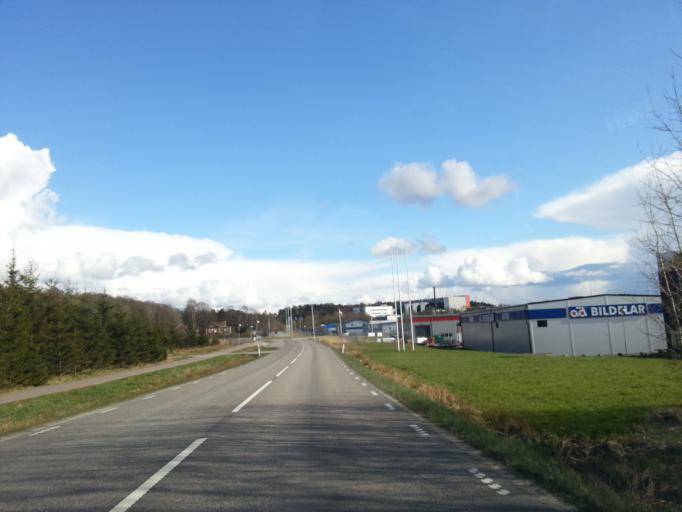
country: SE
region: Vaestra Goetaland
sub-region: Kungalvs Kommun
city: Kungalv
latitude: 57.8925
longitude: 11.9418
